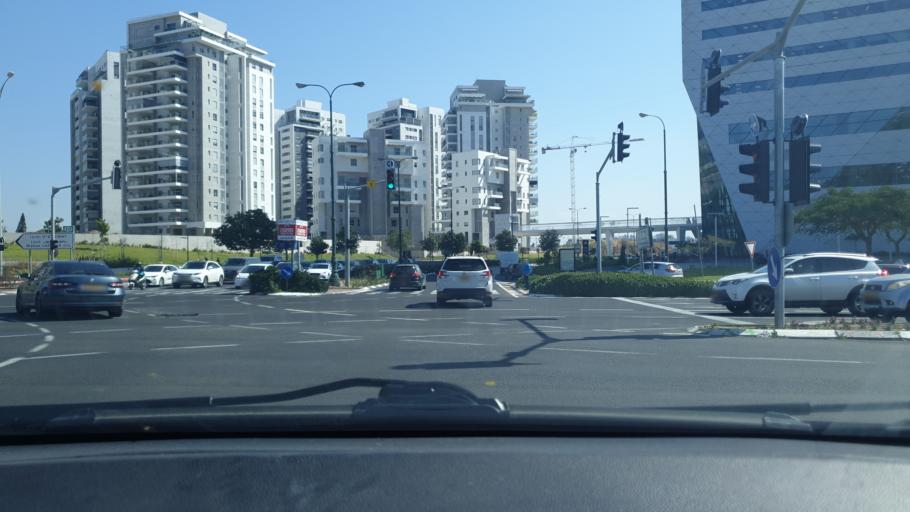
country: IL
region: Central District
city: Ness Ziona
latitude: 31.9507
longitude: 34.8019
